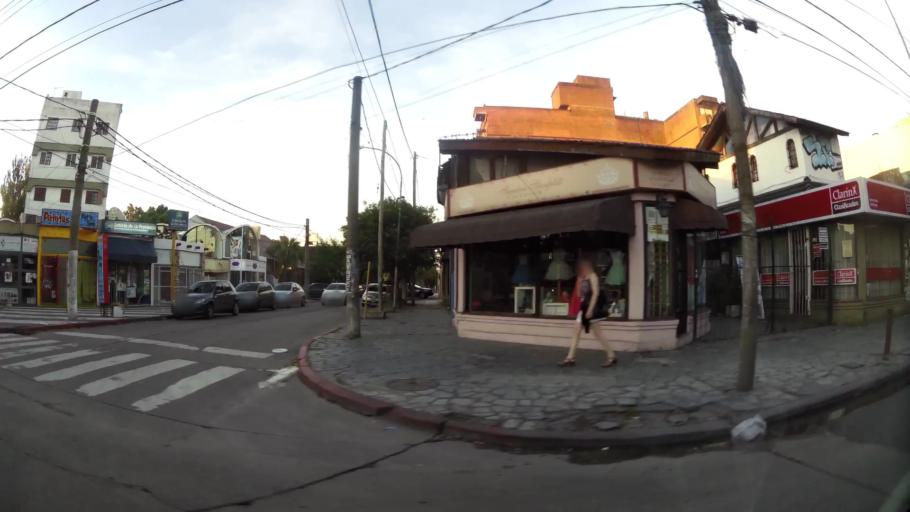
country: AR
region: Buenos Aires
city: Ituzaingo
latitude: -34.6506
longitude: -58.6458
